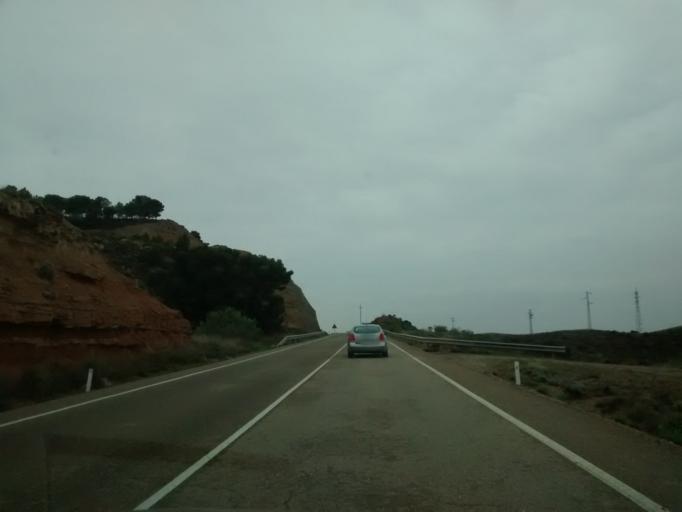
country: ES
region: Aragon
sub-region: Provincia de Zaragoza
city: Caspe
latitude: 41.2653
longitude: -0.0547
